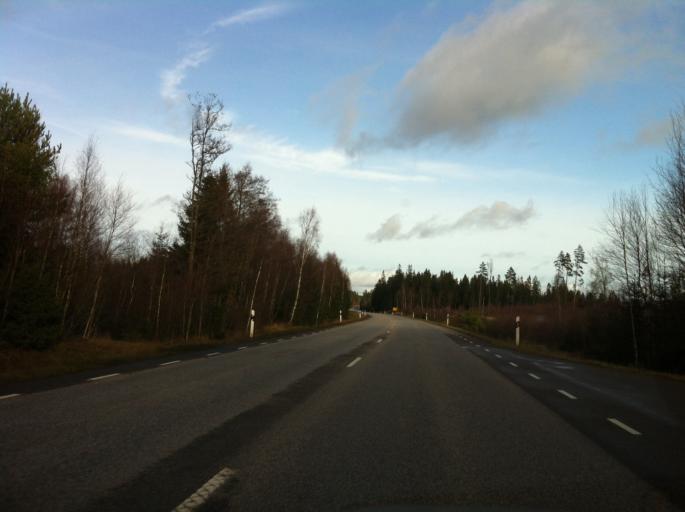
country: SE
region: Kronoberg
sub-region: Almhults Kommun
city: AElmhult
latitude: 56.6000
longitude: 14.2156
